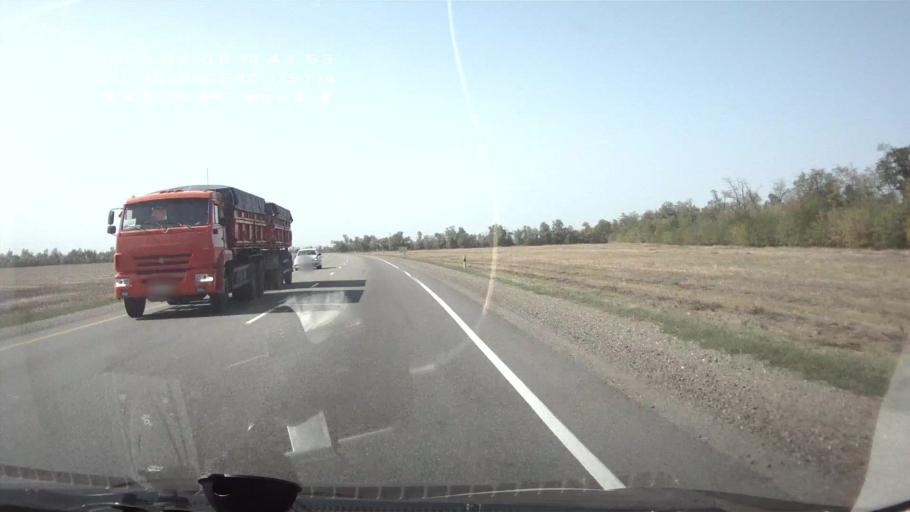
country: RU
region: Krasnodarskiy
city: Tbilisskaya
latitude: 45.4014
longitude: 40.1736
